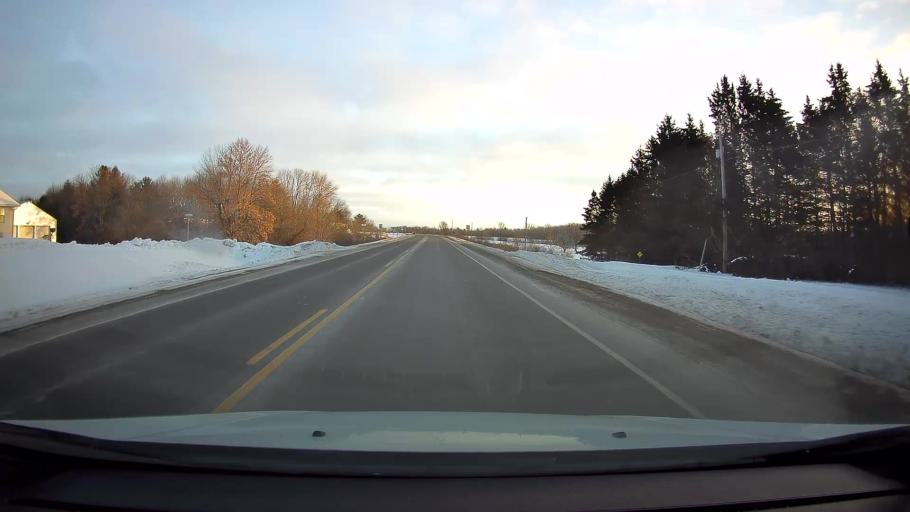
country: US
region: Wisconsin
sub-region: Polk County
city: Clear Lake
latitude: 45.2564
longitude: -92.2692
